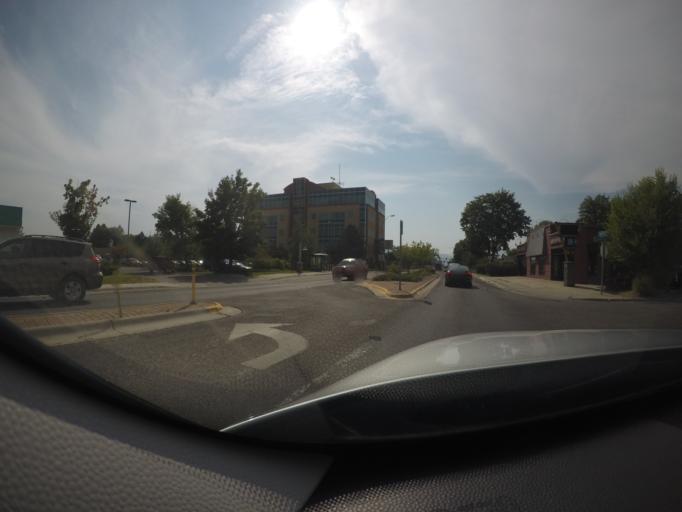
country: US
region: Montana
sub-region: Missoula County
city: Orchard Homes
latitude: 46.8489
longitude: -114.0242
